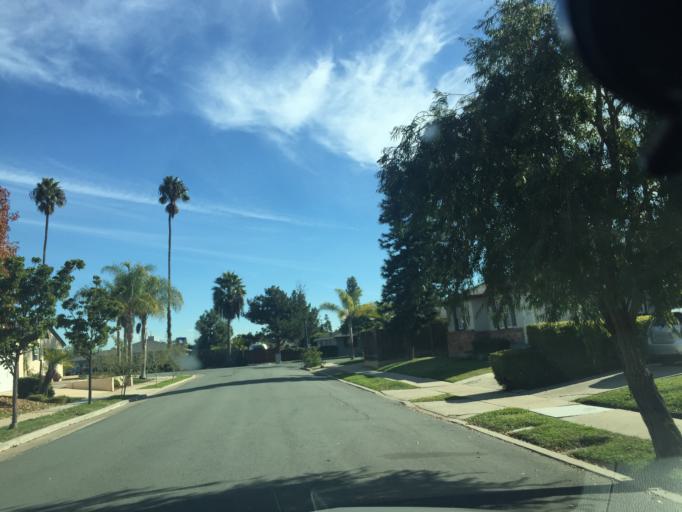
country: US
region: California
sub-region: San Diego County
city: Lemon Grove
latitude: 32.7651
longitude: -117.0862
